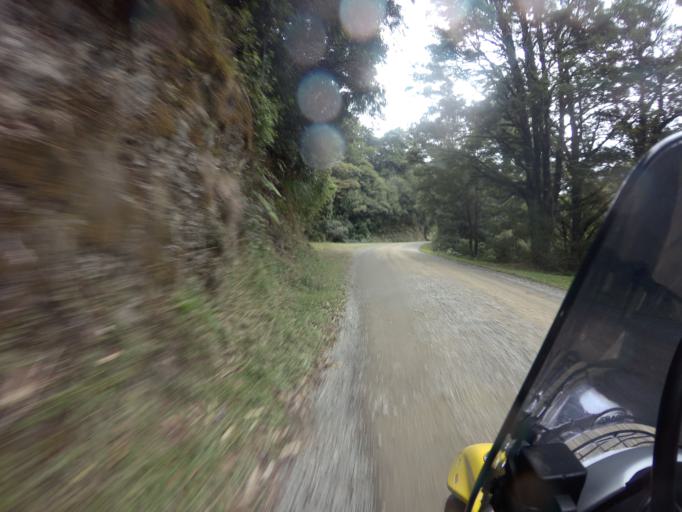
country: NZ
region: Bay of Plenty
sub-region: Whakatane District
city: Murupara
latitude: -38.6640
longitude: 177.0372
